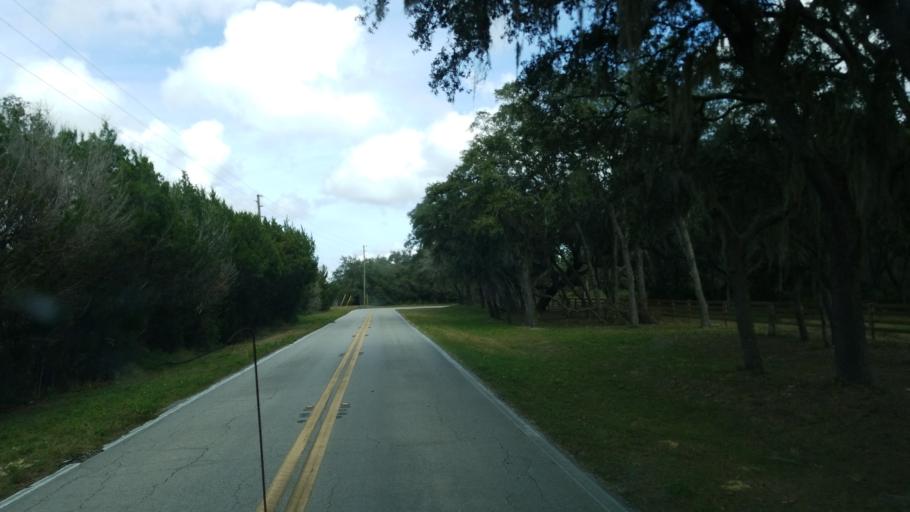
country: US
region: Florida
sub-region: Osceola County
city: Poinciana
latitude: 28.0241
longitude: -81.4961
